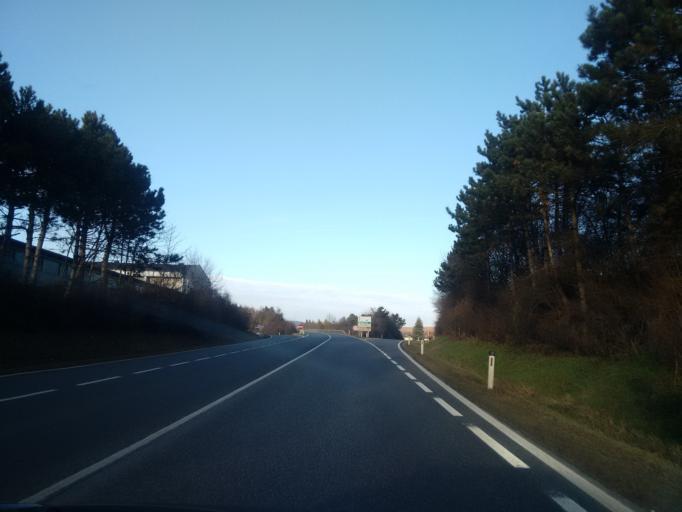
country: AT
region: Lower Austria
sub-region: Politischer Bezirk Melk
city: Melk
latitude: 48.2228
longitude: 15.3497
